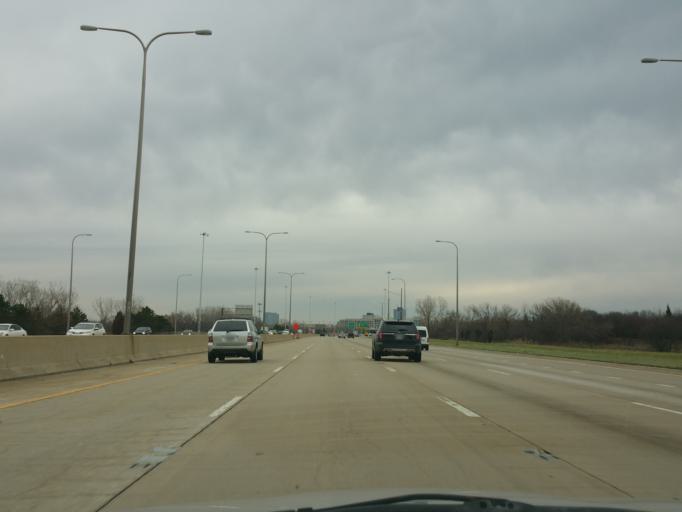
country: US
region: Illinois
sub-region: DuPage County
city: Itasca
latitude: 42.0117
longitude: -88.0293
